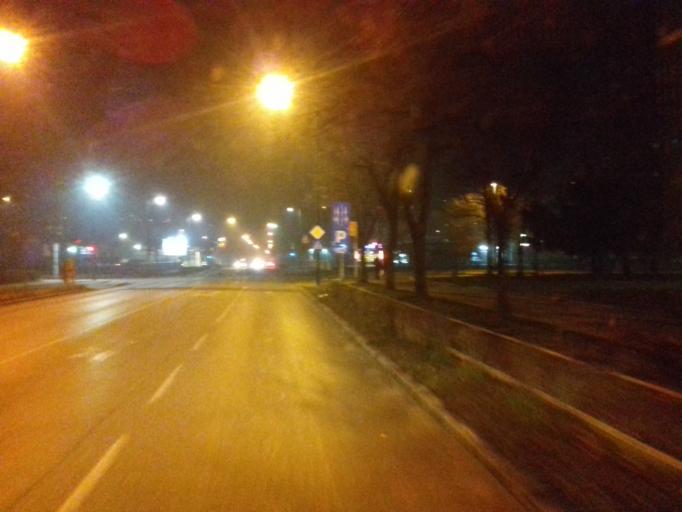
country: BA
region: Federation of Bosnia and Herzegovina
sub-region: Kanton Sarajevo
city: Sarajevo
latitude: 43.8521
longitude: 18.3854
